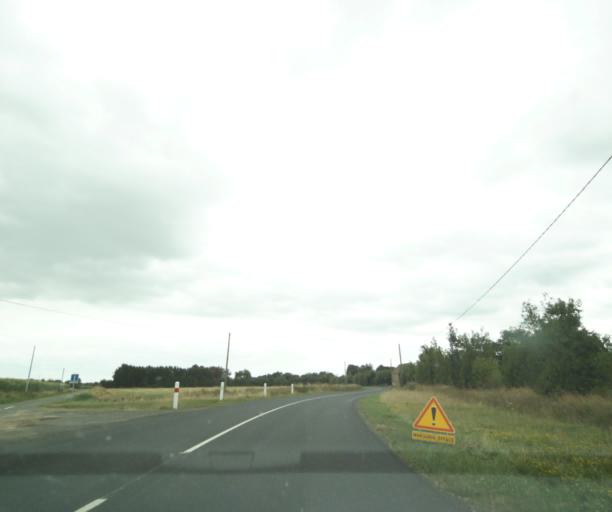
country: FR
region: Pays de la Loire
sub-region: Departement de la Sarthe
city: Precigne
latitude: 47.7622
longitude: -0.3146
